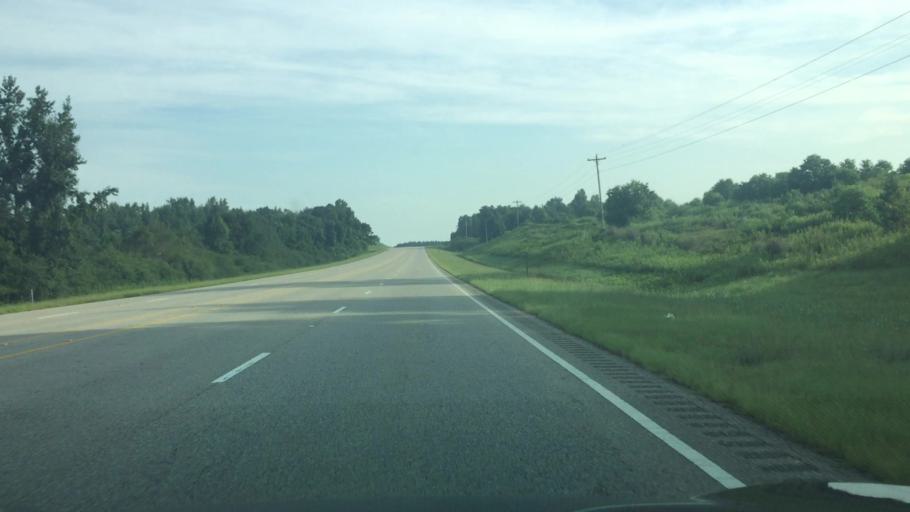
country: US
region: Alabama
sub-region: Covington County
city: Andalusia
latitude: 31.4299
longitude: -86.6116
